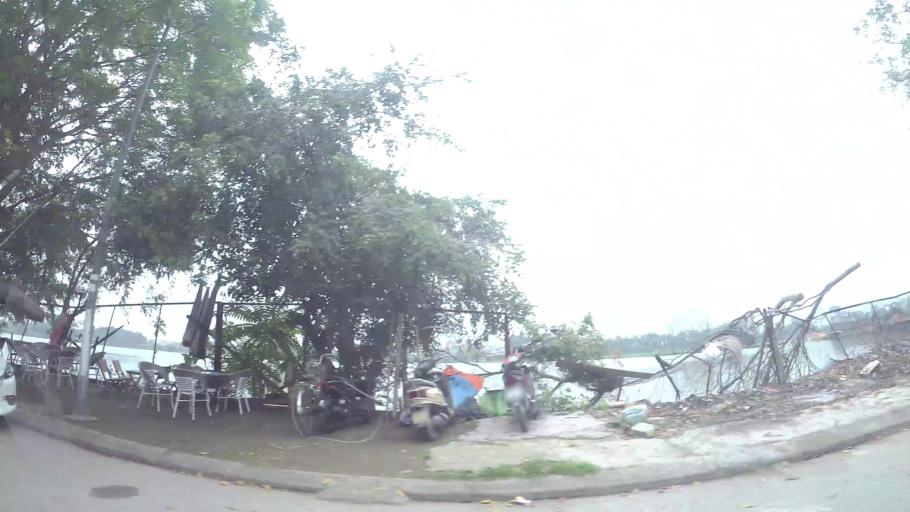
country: VN
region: Ha Noi
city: Van Dien
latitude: 20.9779
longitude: 105.8831
